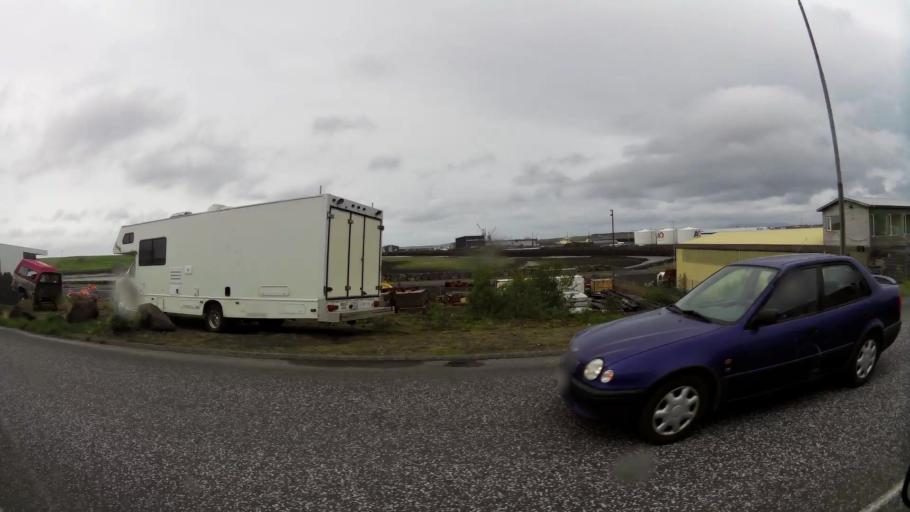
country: IS
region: Capital Region
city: Hafnarfjoerdur
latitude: 64.0611
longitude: -21.9762
